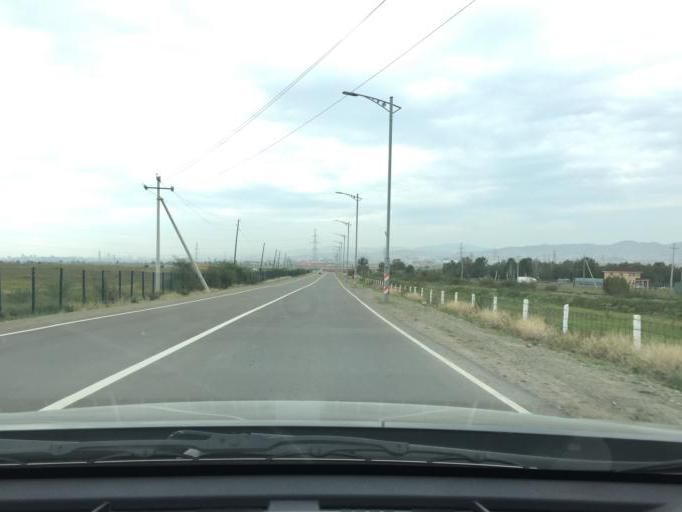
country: MN
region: Ulaanbaatar
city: Ulaanbaatar
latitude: 47.8891
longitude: 107.0445
